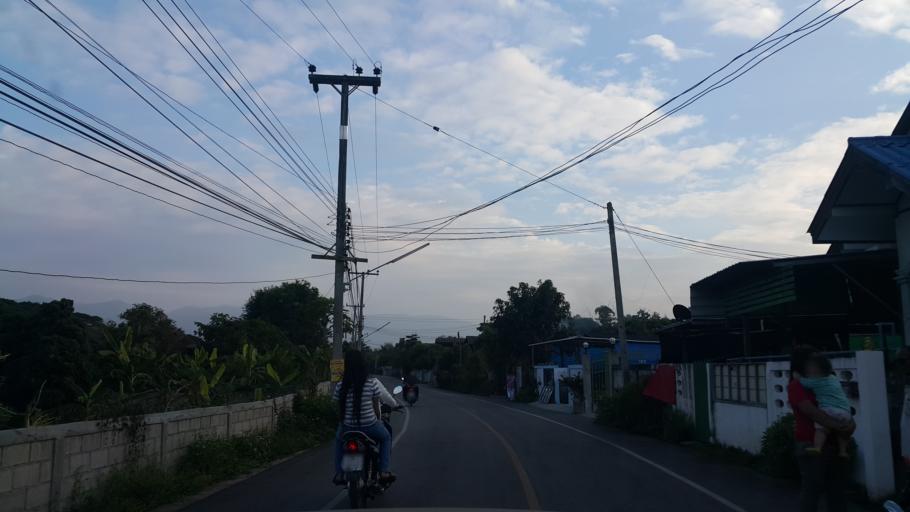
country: TH
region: Lampang
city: Sop Prap
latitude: 17.8922
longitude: 99.3322
